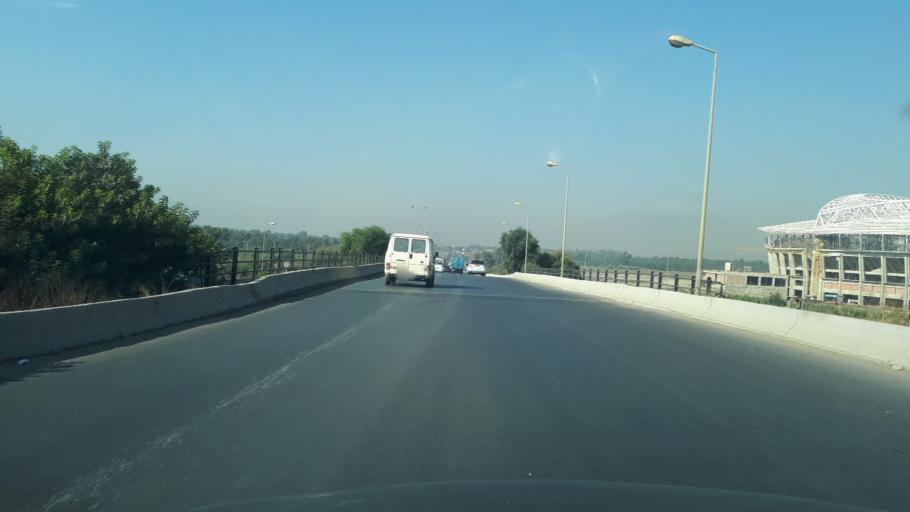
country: DZ
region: Tipaza
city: Baraki
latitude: 36.6934
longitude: 3.1268
